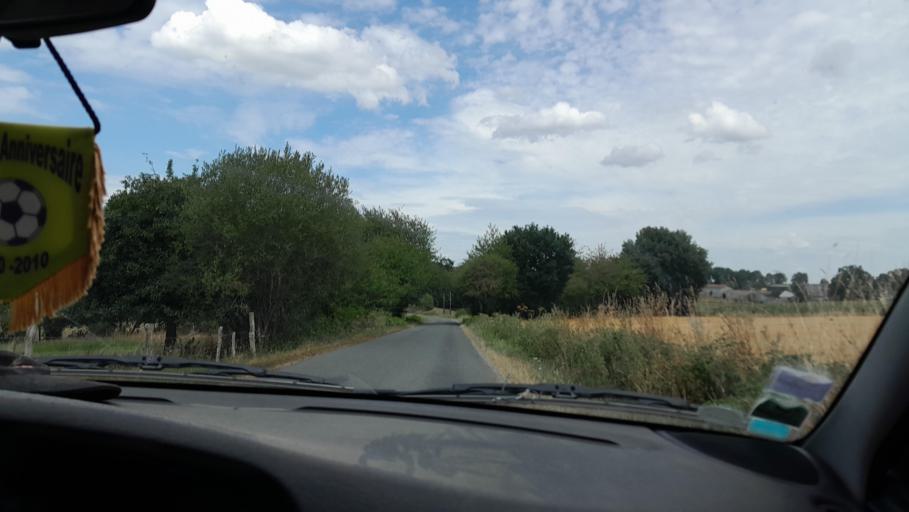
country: FR
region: Pays de la Loire
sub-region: Departement de la Mayenne
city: Juvigne
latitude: 48.1738
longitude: -1.0388
